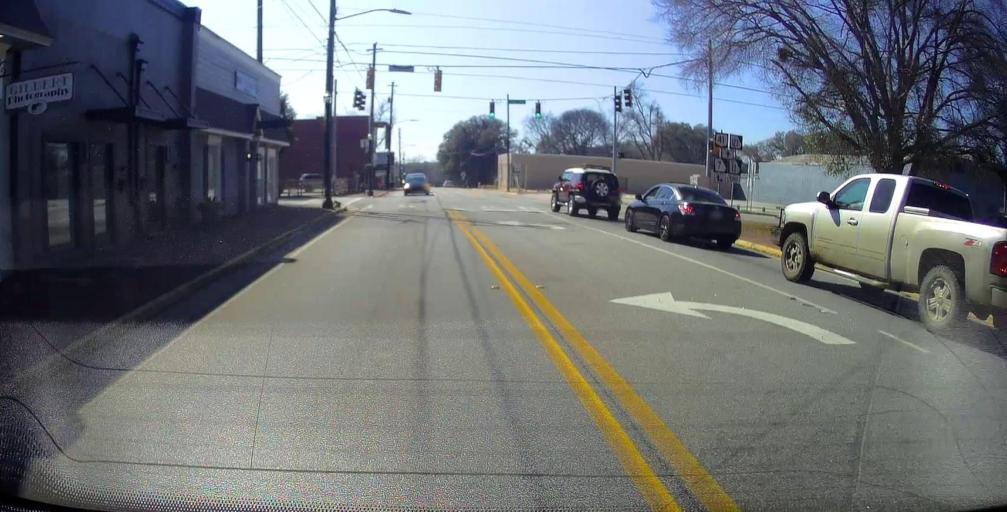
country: US
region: Georgia
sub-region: Houston County
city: Perry
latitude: 32.4592
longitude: -83.7335
